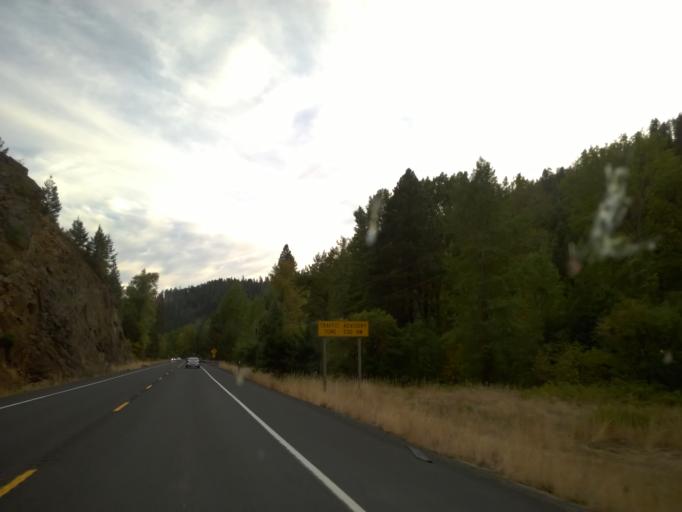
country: US
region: Washington
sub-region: Kittitas County
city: Cle Elum
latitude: 47.2215
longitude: -120.6979
